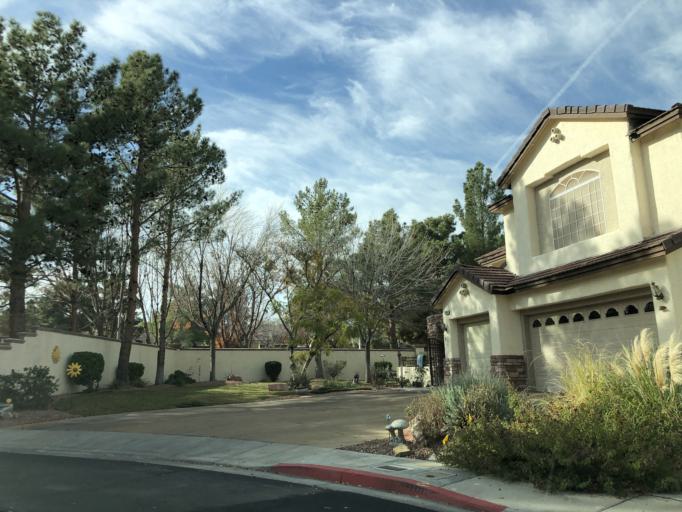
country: US
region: Nevada
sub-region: Clark County
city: Whitney
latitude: 36.0189
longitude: -115.0758
